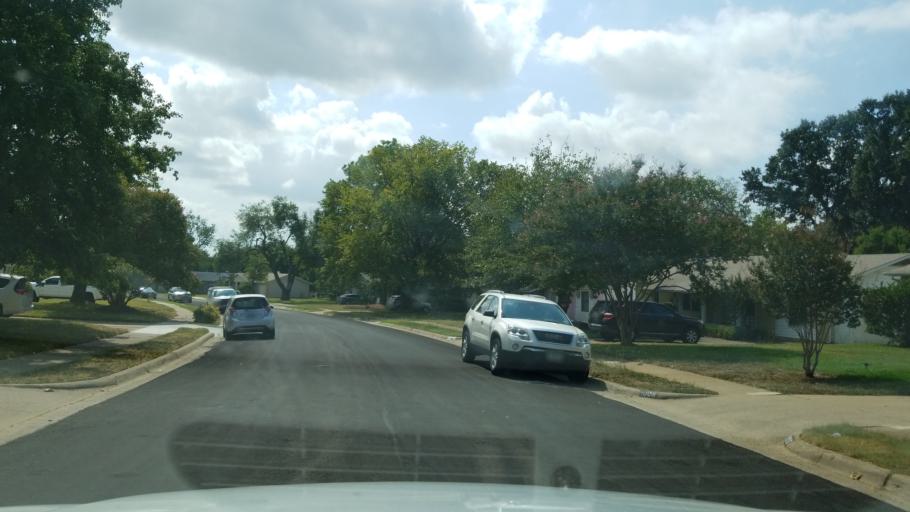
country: US
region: Texas
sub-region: Tarrant County
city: Euless
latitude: 32.8508
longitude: -97.0926
